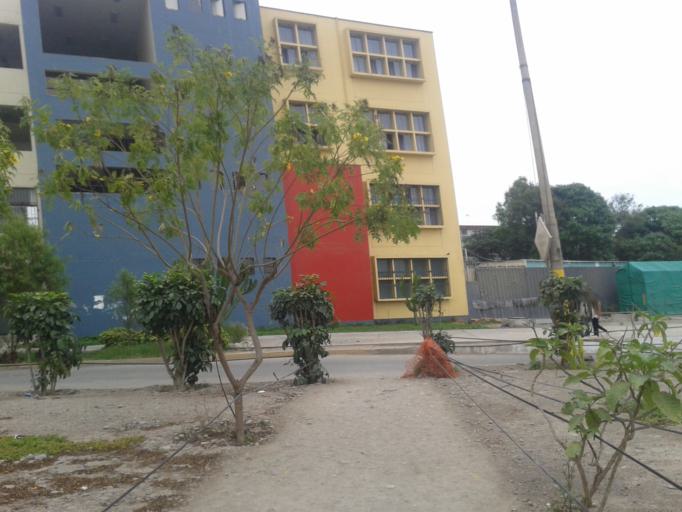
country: PE
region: Callao
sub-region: Callao
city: Callao
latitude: -12.0590
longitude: -77.0822
